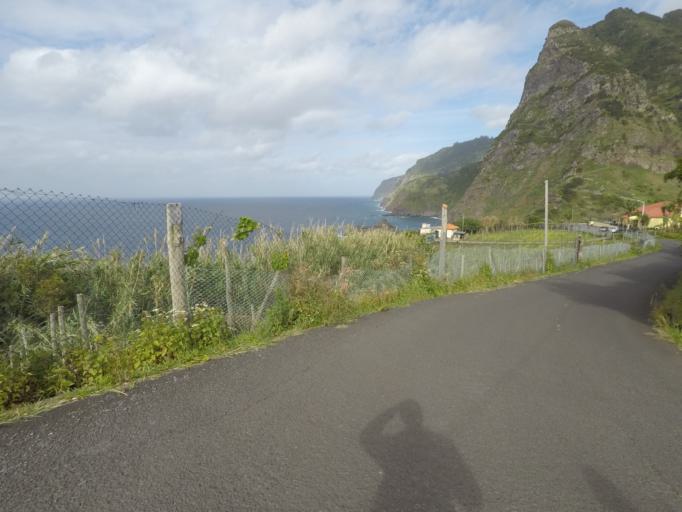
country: PT
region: Madeira
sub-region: Sao Vicente
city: Sao Vicente
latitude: 32.8275
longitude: -16.9745
